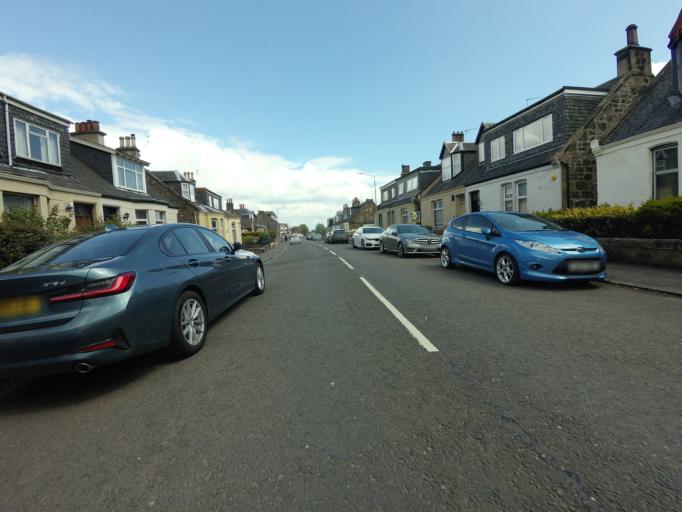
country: GB
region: Scotland
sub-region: Falkirk
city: Falkirk
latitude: 56.0129
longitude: -3.7909
